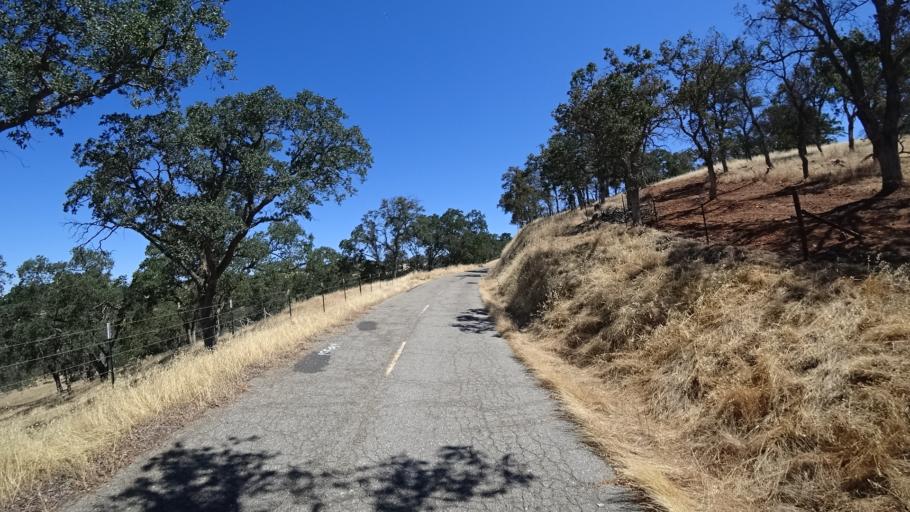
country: US
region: California
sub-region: Calaveras County
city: Copperopolis
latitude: 37.9379
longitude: -120.7342
